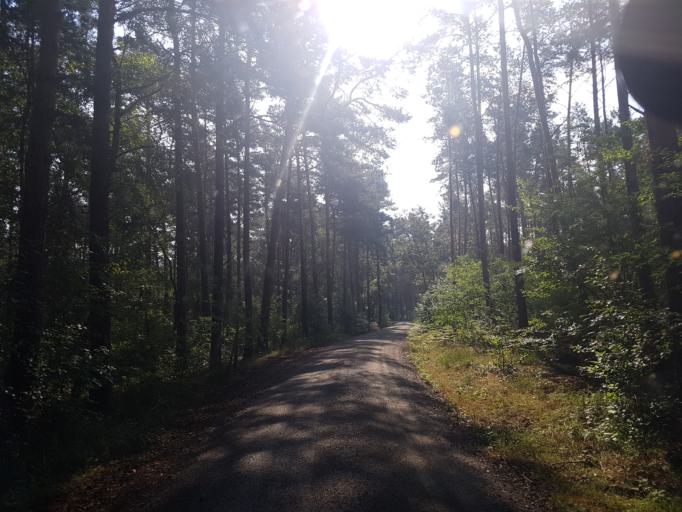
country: DE
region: Brandenburg
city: Hohenleipisch
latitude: 51.5147
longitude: 13.5841
